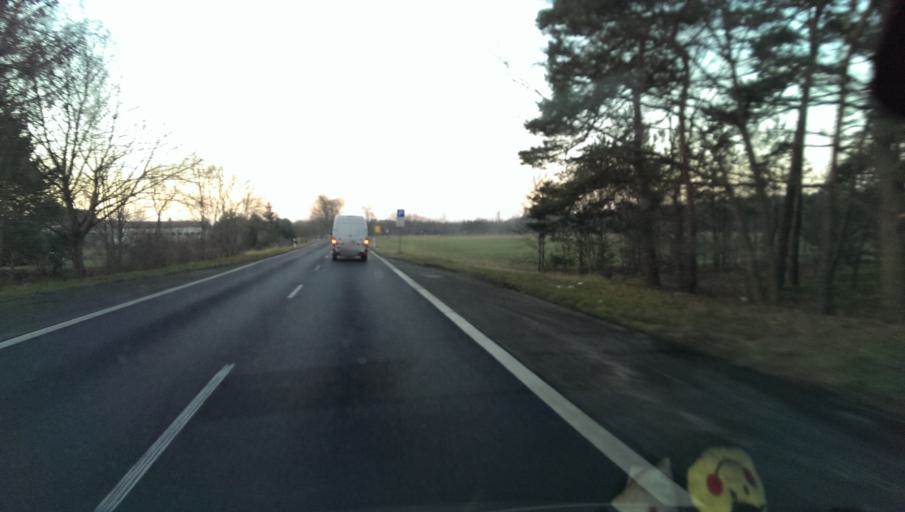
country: DE
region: Brandenburg
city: Herzberg
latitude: 51.7357
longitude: 13.2091
